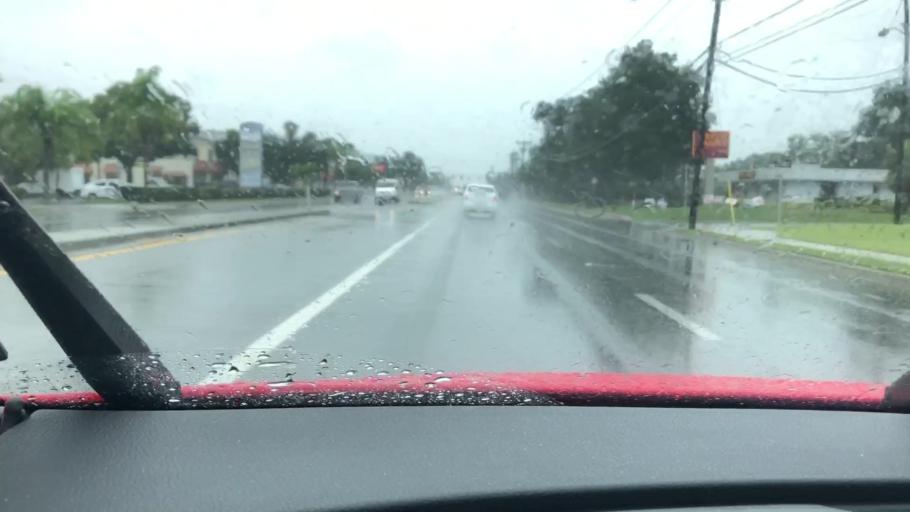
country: US
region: Florida
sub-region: Volusia County
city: South Daytona
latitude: 29.1726
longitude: -81.0351
